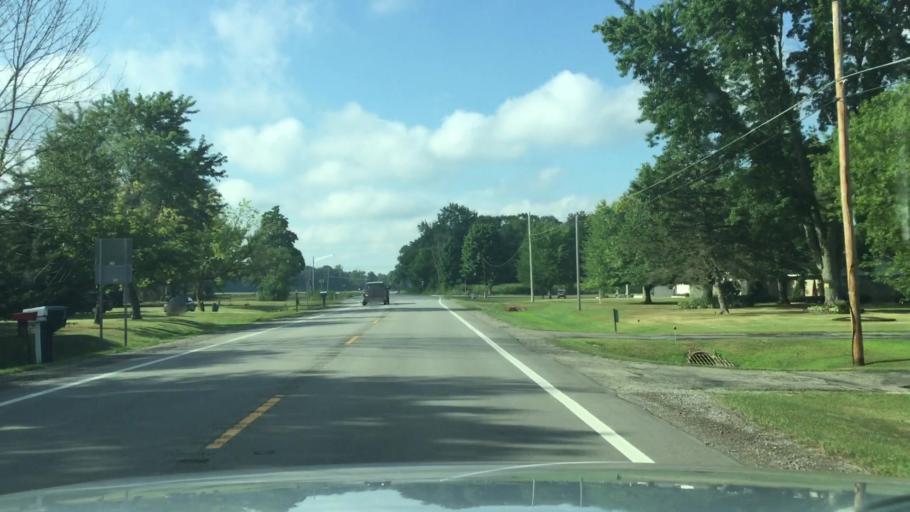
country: US
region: Michigan
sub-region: Genesee County
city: Clio
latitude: 43.2229
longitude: -83.7352
